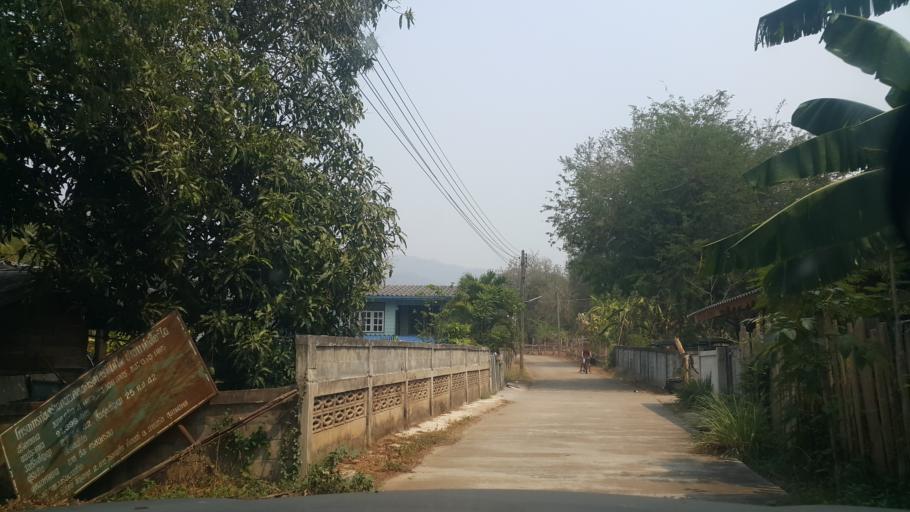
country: TH
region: Lampang
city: Sop Prap
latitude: 17.8052
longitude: 99.2567
